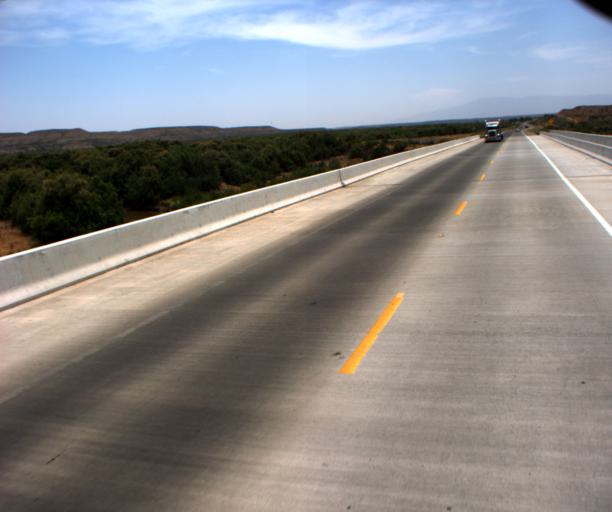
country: US
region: Arizona
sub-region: Graham County
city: Bylas
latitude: 33.1637
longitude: -110.1335
